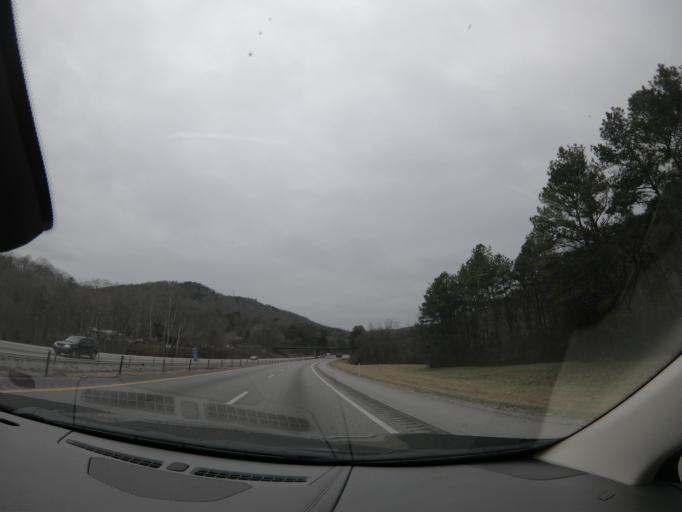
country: US
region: Georgia
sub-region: Dade County
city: Trenton
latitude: 34.9893
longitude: -85.5071
